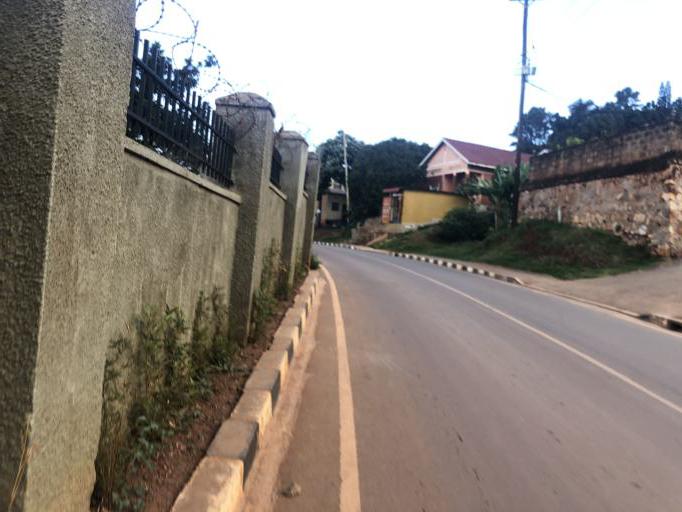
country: UG
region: Central Region
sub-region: Kampala District
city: Kampala
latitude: 0.2769
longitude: 32.5989
